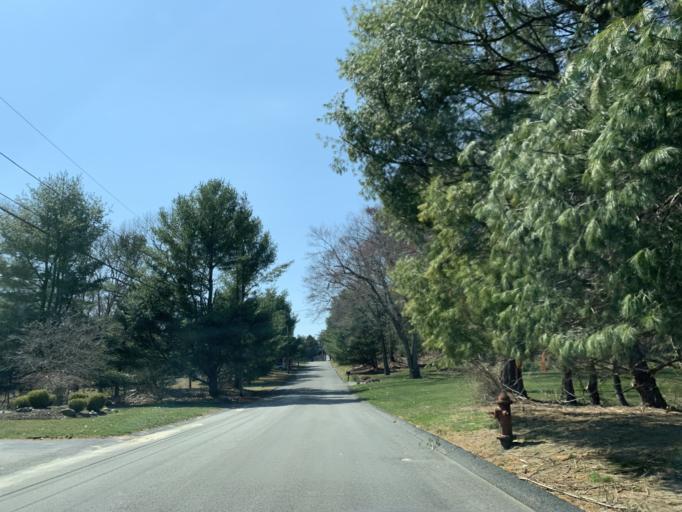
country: US
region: Rhode Island
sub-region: Kent County
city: East Greenwich
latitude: 41.6322
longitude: -71.4314
